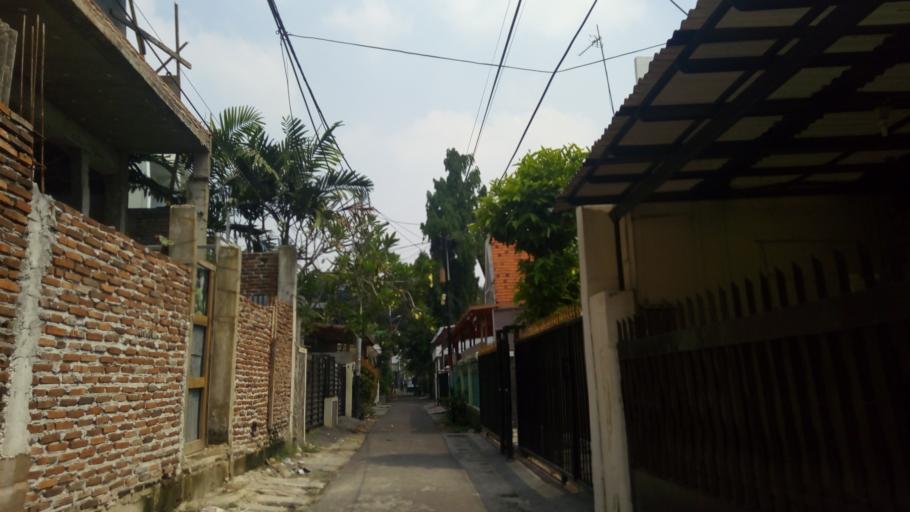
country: ID
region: Jakarta Raya
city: Jakarta
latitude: -6.2024
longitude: 106.8257
